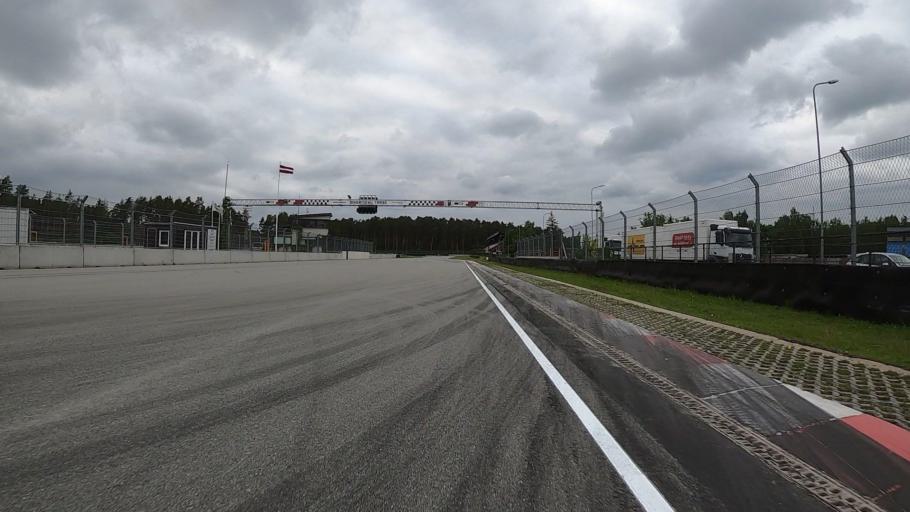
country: LV
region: Stopini
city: Ulbroka
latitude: 56.9644
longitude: 24.2296
